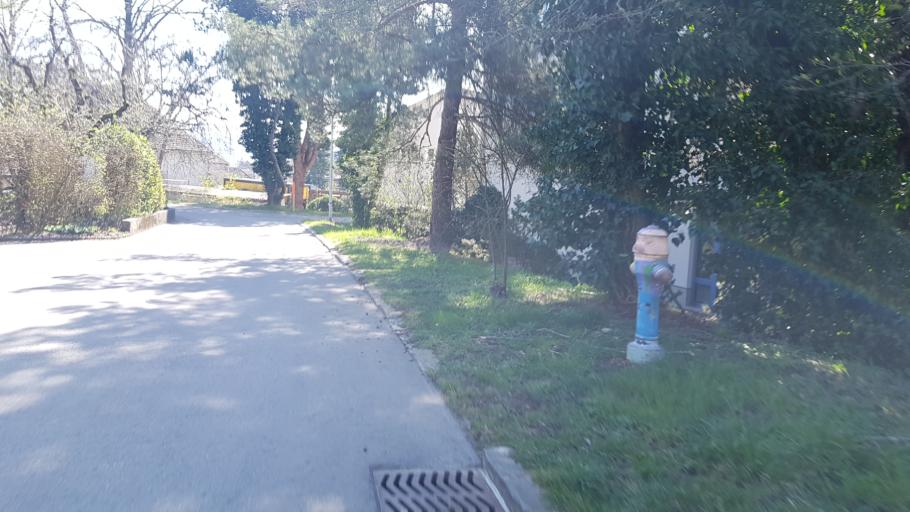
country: CH
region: Aargau
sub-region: Bezirk Kulm
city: Reinach
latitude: 47.2681
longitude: 8.1988
